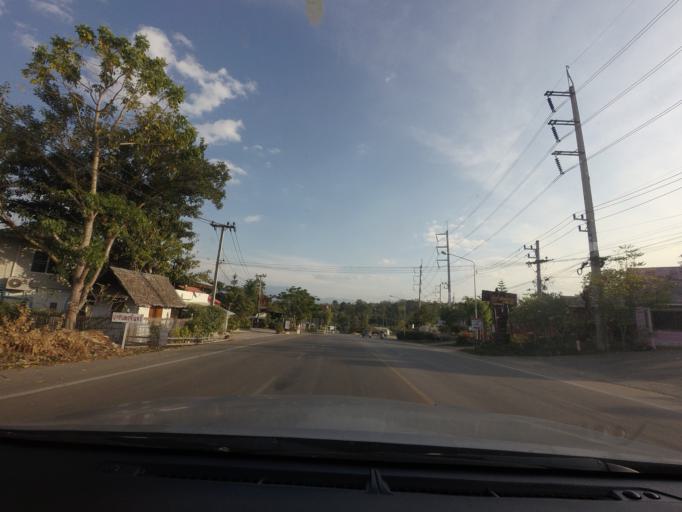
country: TH
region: Chiang Mai
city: Pai
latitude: 19.3466
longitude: 98.4327
